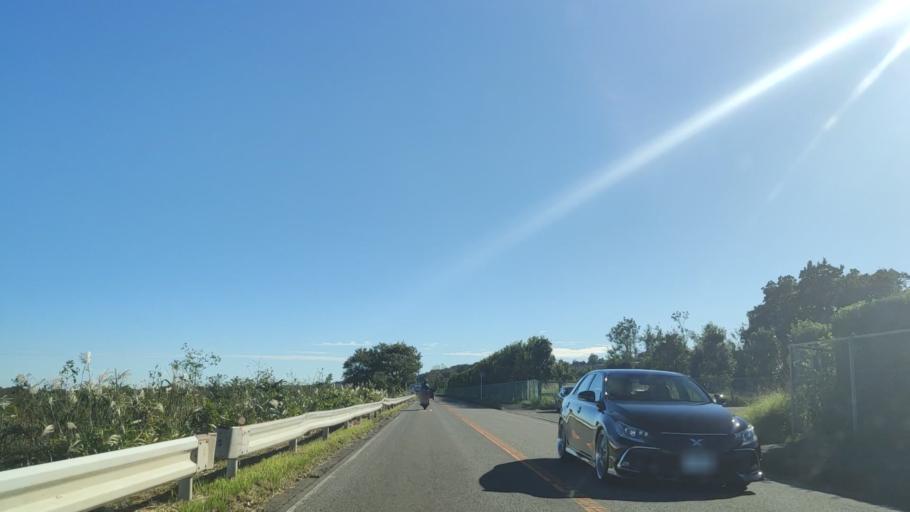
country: JP
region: Kanagawa
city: Zama
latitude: 35.5020
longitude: 139.3720
